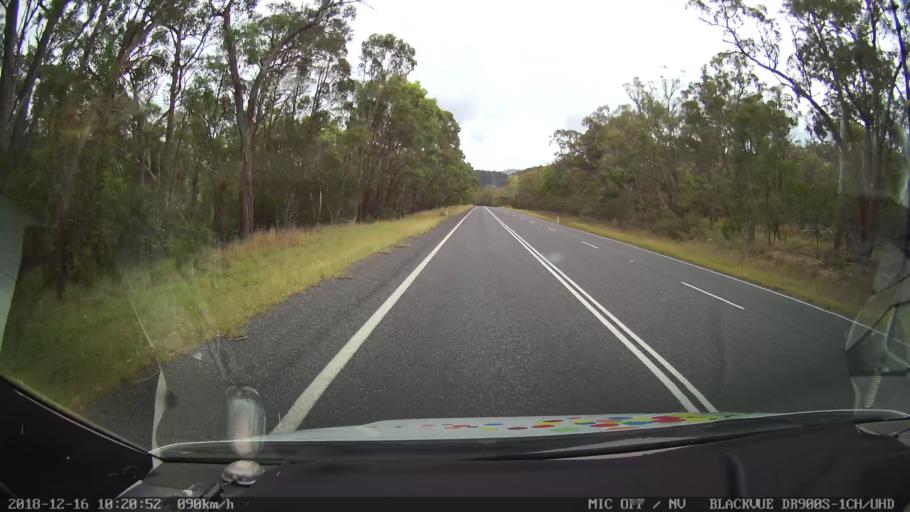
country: AU
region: New South Wales
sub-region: Tenterfield Municipality
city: Carrolls Creek
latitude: -29.2146
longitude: 152.0108
